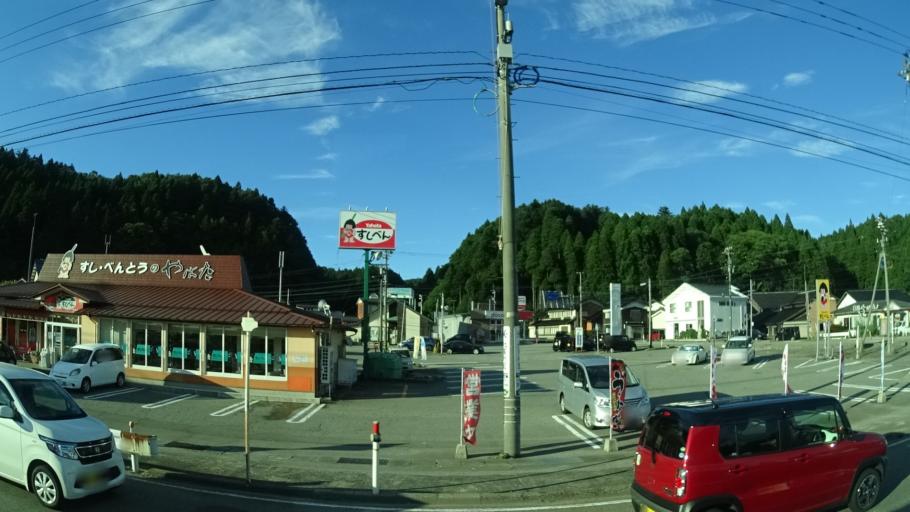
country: JP
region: Ishikawa
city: Nanao
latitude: 37.2441
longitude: 136.8987
